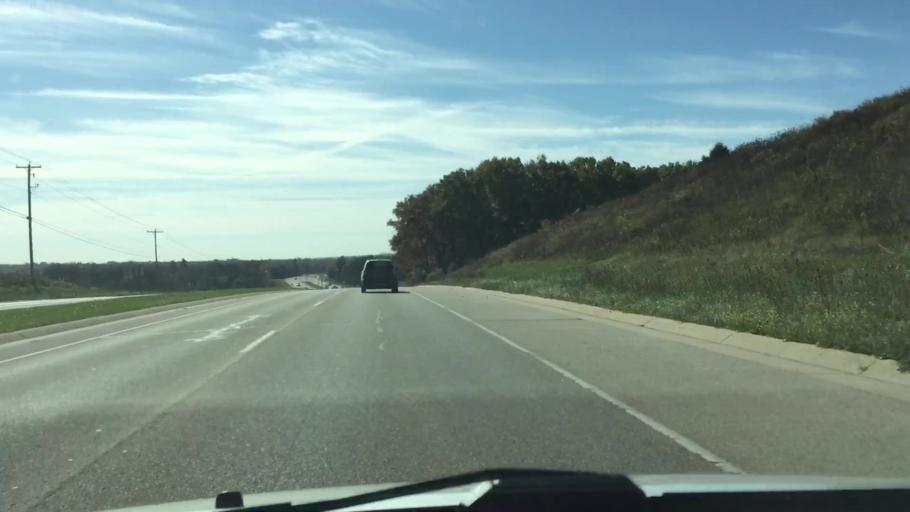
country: US
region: Wisconsin
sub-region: Waukesha County
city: Pewaukee
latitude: 43.1083
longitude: -88.2449
